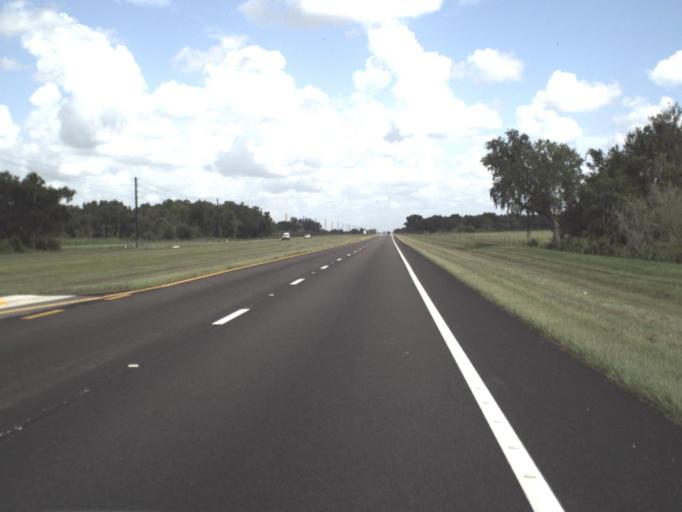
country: US
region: Florida
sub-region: Hardee County
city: Zolfo Springs
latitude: 27.4233
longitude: -81.7957
